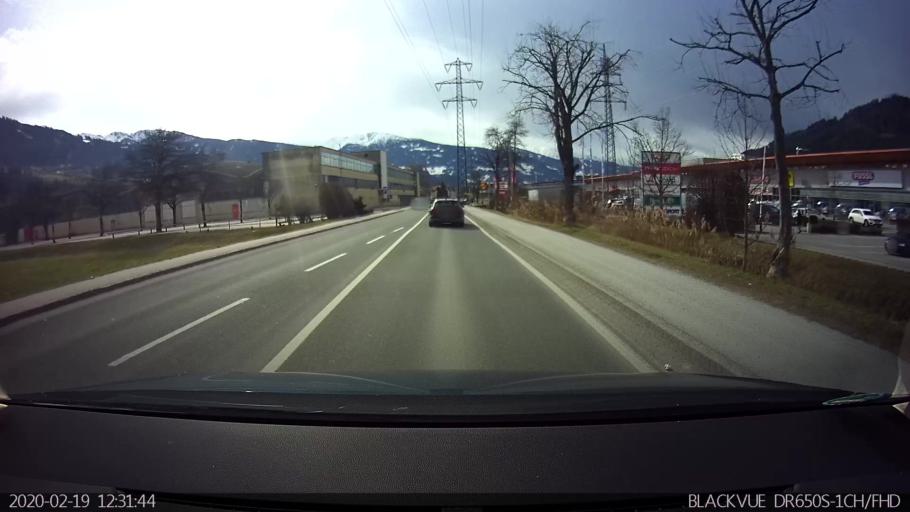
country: AT
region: Tyrol
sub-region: Politischer Bezirk Schwaz
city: Schwaz
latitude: 47.3503
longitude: 11.6982
